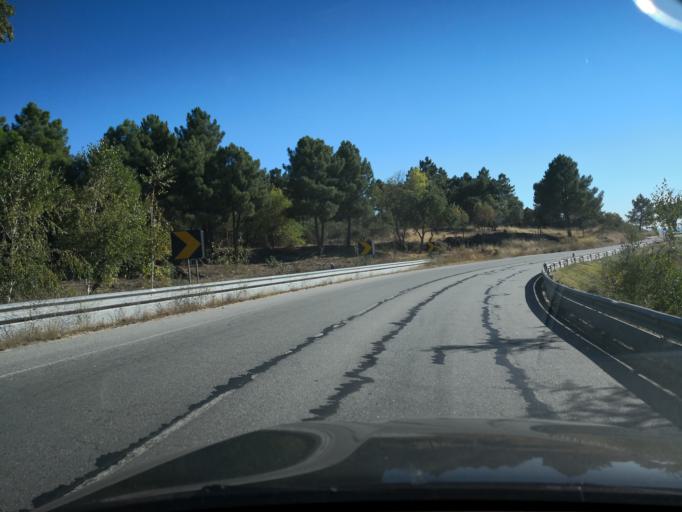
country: PT
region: Vila Real
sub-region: Valpacos
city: Valpacos
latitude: 41.6399
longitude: -7.3161
